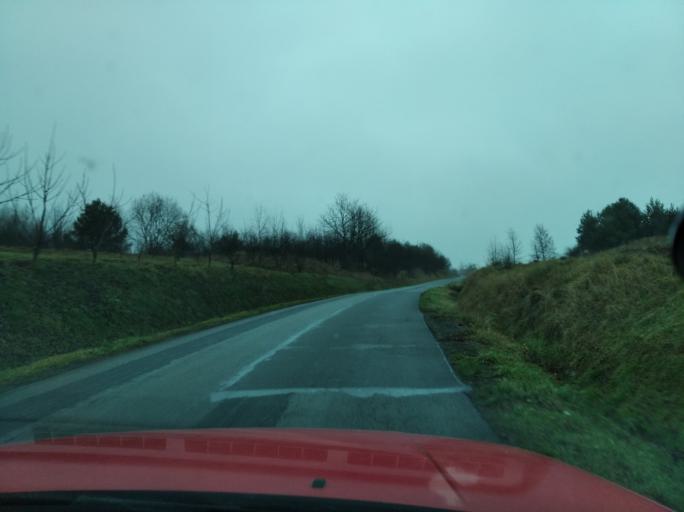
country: PL
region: Subcarpathian Voivodeship
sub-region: Powiat przemyski
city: Nienadowa
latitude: 49.8736
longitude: 22.4216
